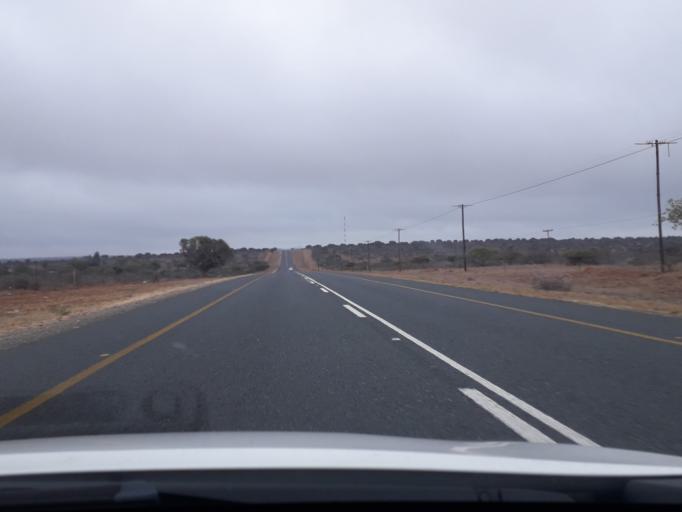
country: ZA
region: Limpopo
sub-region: Vhembe District Municipality
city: Louis Trichardt
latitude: -23.4149
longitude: 29.7536
